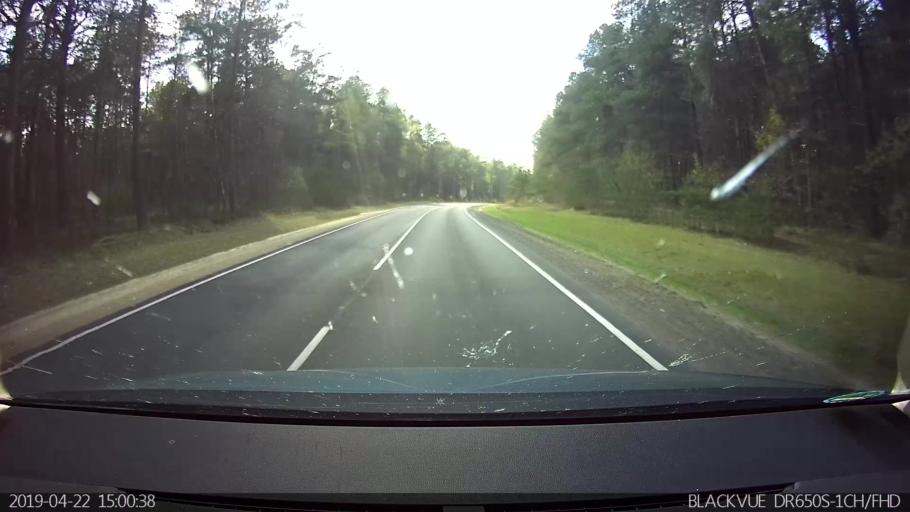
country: BY
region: Brest
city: Zhabinka
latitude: 52.3526
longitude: 23.9892
